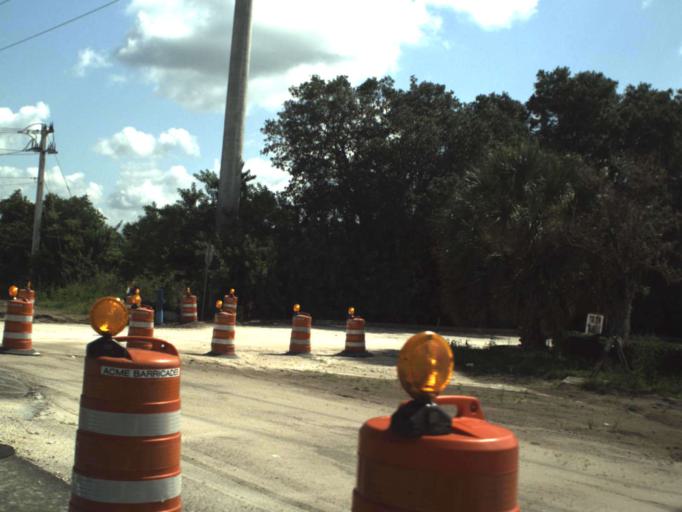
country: US
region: Florida
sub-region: Seminole County
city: Midway
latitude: 28.7875
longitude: -81.2128
